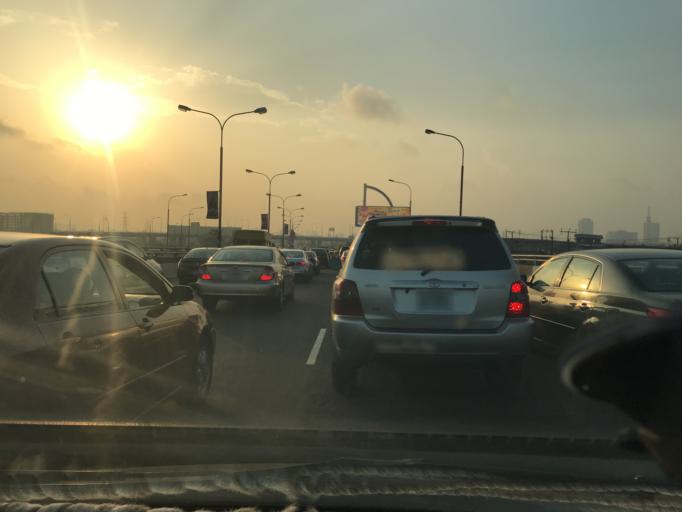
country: NG
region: Lagos
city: Lagos
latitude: 6.4638
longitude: 3.3933
